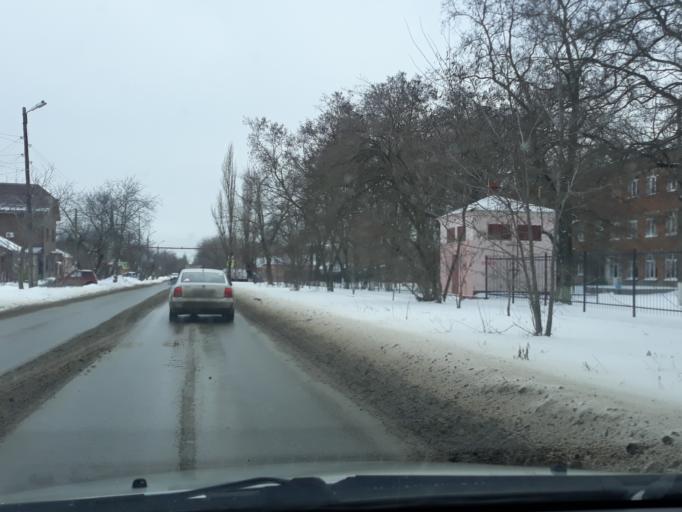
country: RU
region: Rostov
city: Taganrog
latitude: 47.2421
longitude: 38.8770
